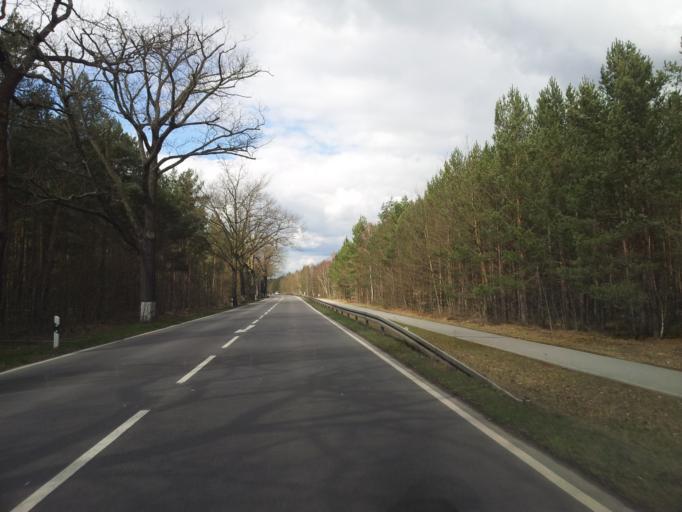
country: DE
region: Saxony
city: Wittichenau
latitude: 51.4095
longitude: 14.2893
